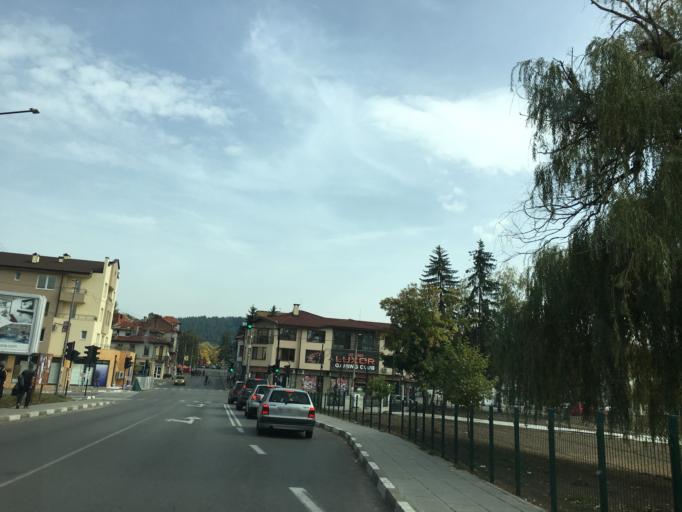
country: BG
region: Sofiya
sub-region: Obshtina Samokov
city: Samokov
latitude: 42.3370
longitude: 23.5546
